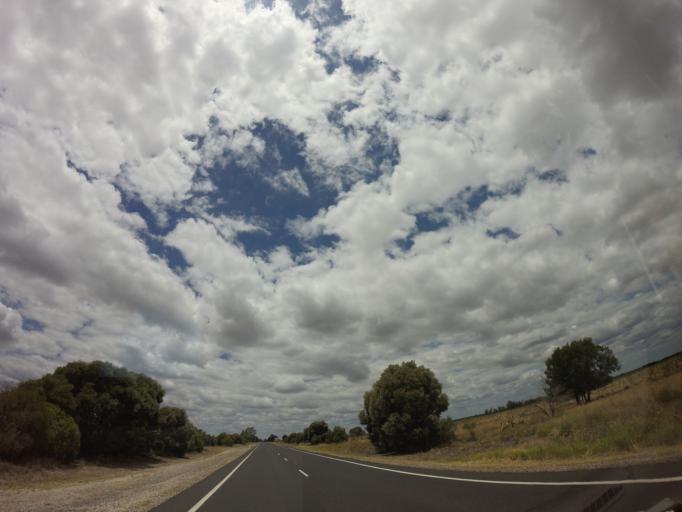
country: AU
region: Queensland
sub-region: Goondiwindi
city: Goondiwindi
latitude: -28.1742
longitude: 150.4900
